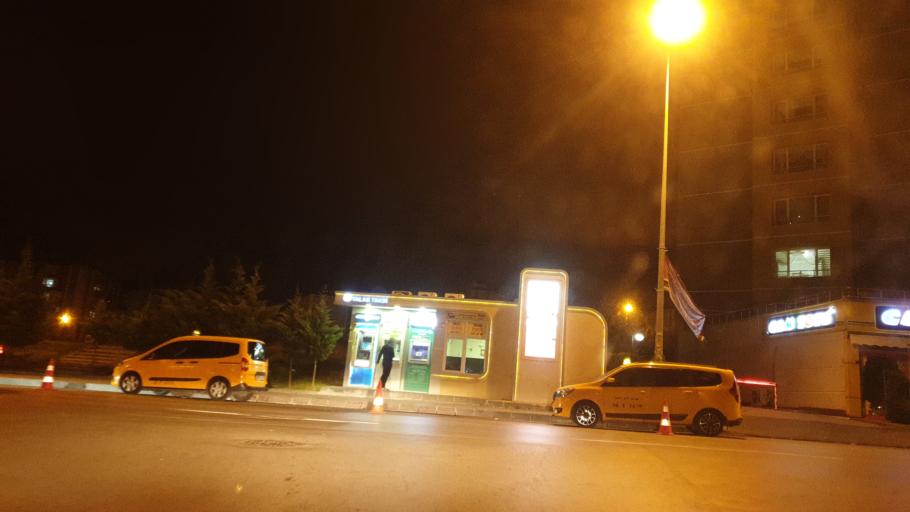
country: TR
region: Kayseri
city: Talas
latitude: 38.6929
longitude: 35.5451
